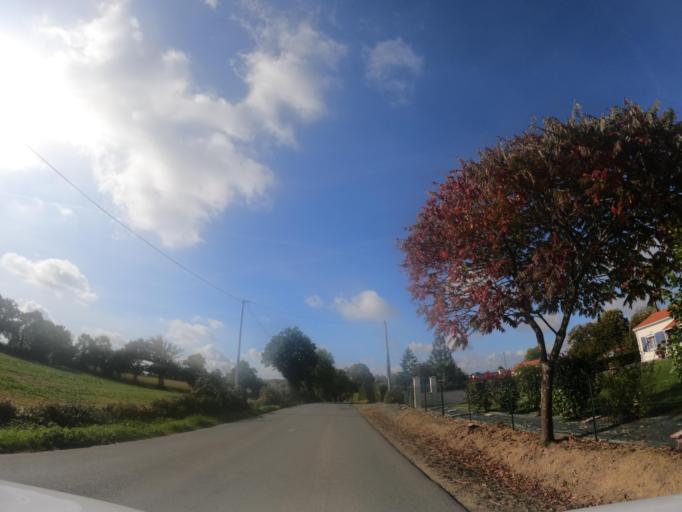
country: FR
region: Poitou-Charentes
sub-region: Departement des Deux-Sevres
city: Courlay
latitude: 46.7866
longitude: -0.5971
